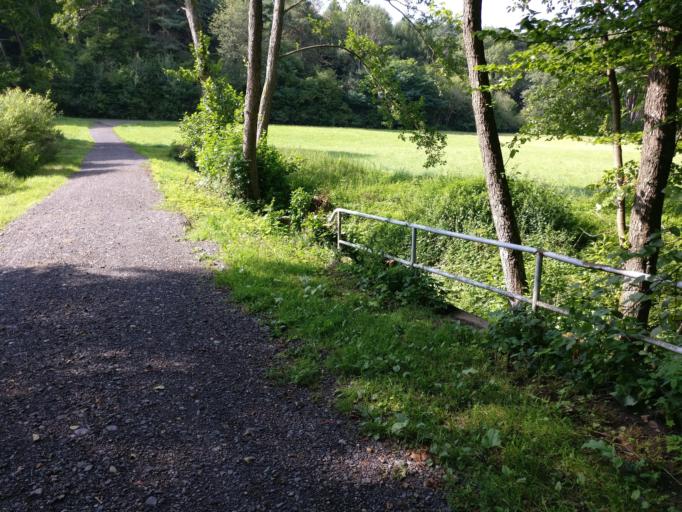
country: DE
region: Hesse
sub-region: Regierungsbezirk Giessen
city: Merkenbach
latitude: 50.6407
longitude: 8.2993
